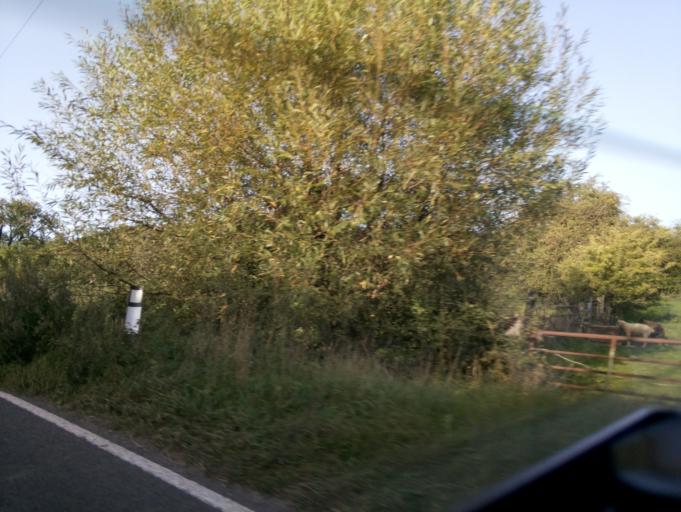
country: GB
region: England
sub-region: Gloucestershire
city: Gloucester
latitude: 51.9336
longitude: -2.2942
